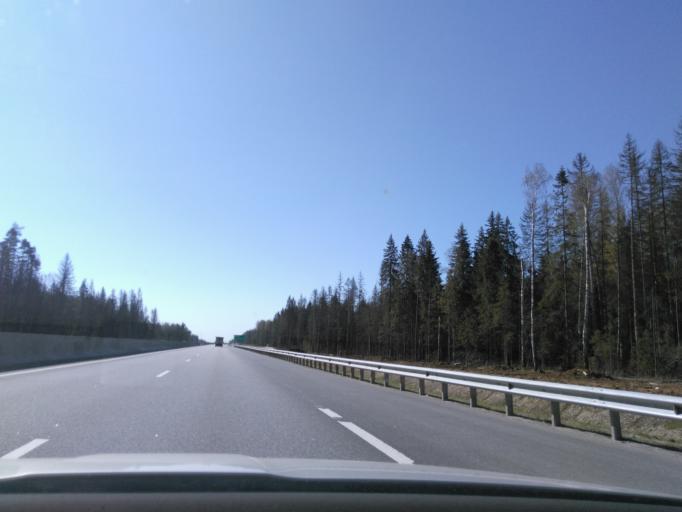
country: RU
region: Moskovskaya
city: Rzhavki
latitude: 56.0203
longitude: 37.2777
